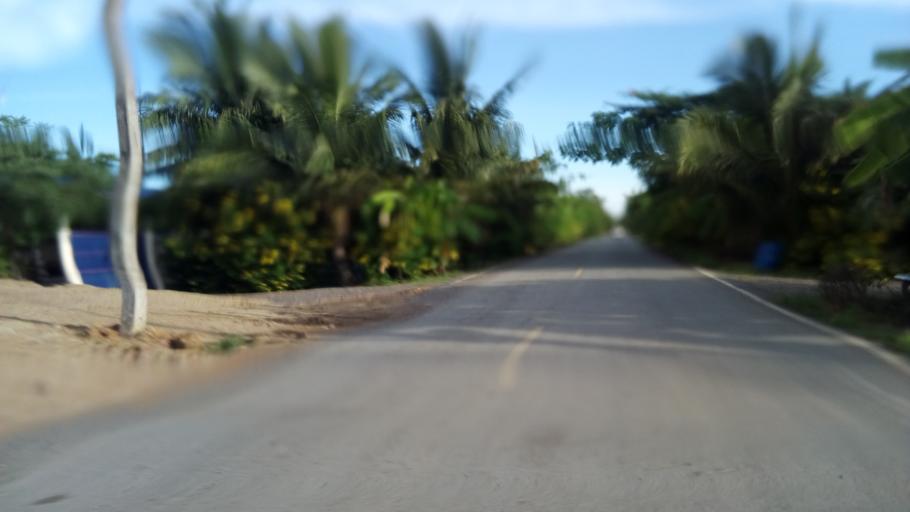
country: TH
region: Pathum Thani
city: Ban Lam Luk Ka
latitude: 14.0261
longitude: 100.8471
